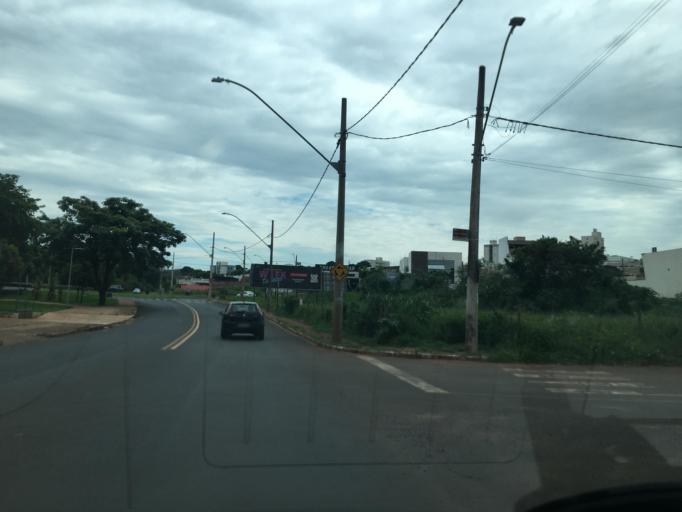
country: BR
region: Minas Gerais
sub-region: Uberlandia
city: Uberlandia
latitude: -18.9188
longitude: -48.3036
